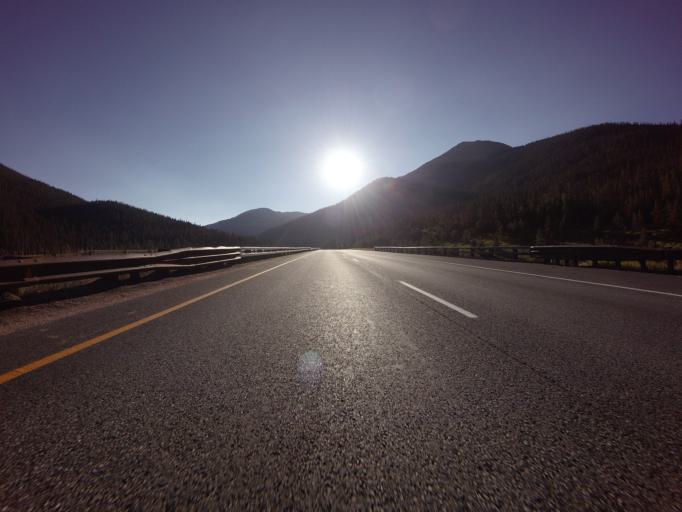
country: US
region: Colorado
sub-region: Clear Creek County
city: Georgetown
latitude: 39.7017
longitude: -105.8569
